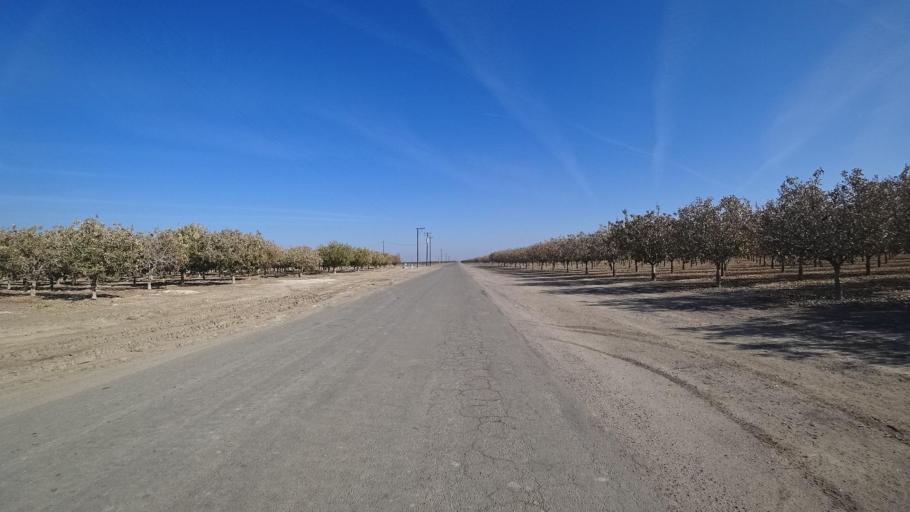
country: US
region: California
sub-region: Kern County
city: Wasco
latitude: 35.6886
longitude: -119.4254
